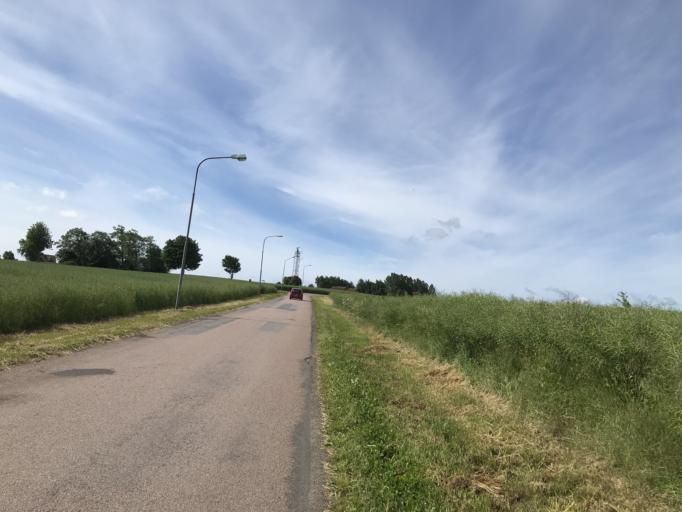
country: SE
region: Skane
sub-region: Helsingborg
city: Glumslov
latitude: 55.9365
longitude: 12.8028
